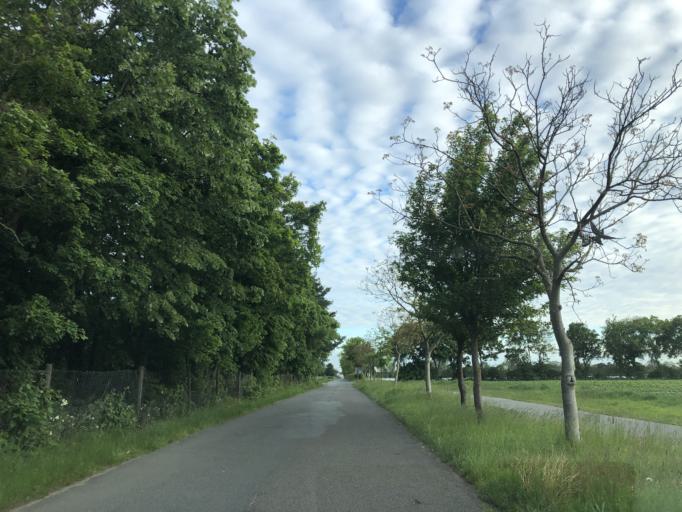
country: DE
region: Hesse
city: Weiterstadt
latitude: 49.9419
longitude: 8.6033
